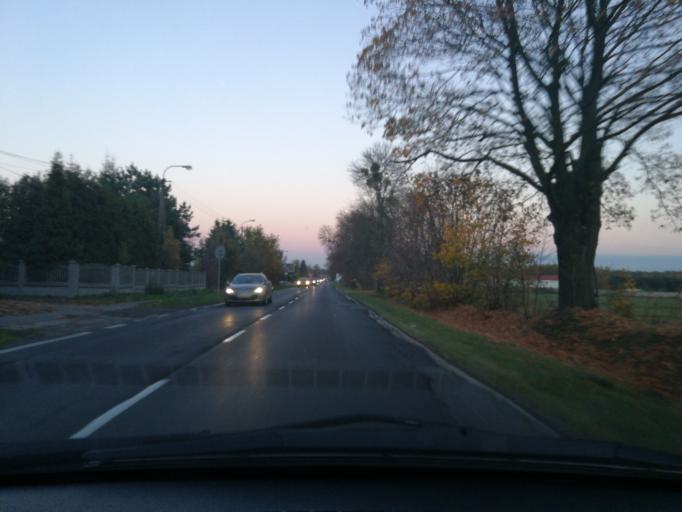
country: PL
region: Lodz Voivodeship
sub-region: Powiat lodzki wschodni
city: Andrespol
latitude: 51.7931
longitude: 19.6023
